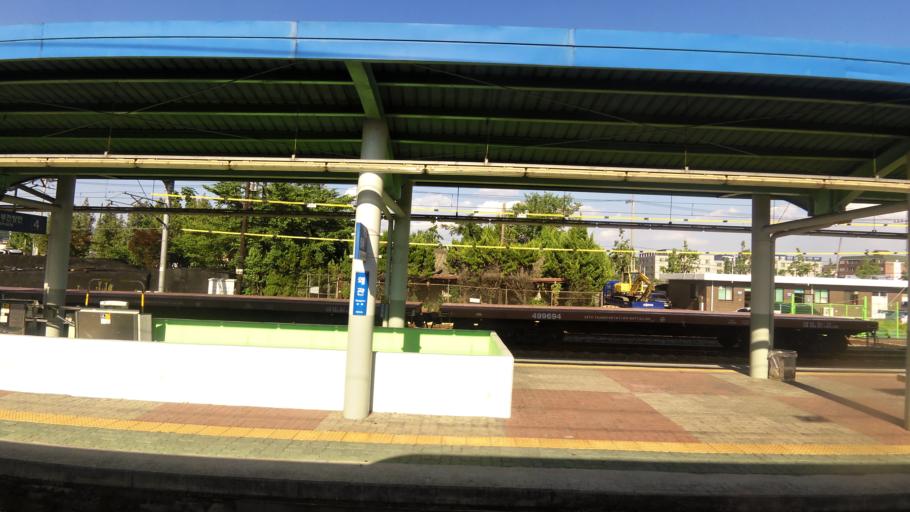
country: KR
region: Gyeongsangbuk-do
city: Waegwan
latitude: 35.9919
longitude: 128.4005
